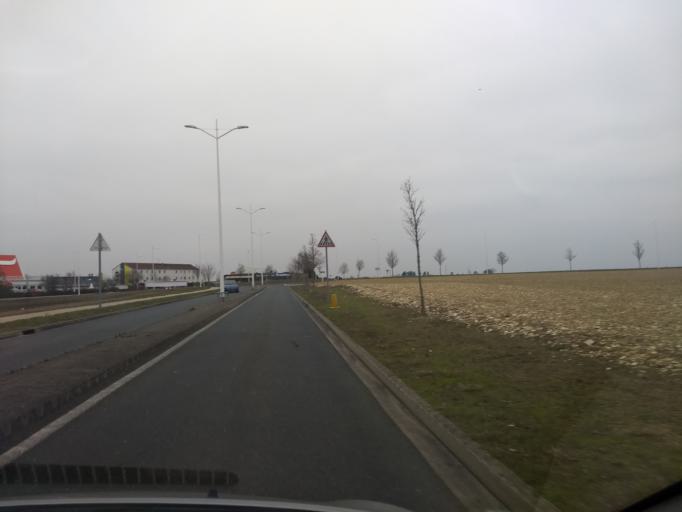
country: FR
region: Centre
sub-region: Departement de l'Indre
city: Deols
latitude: 46.8509
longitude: 1.7074
